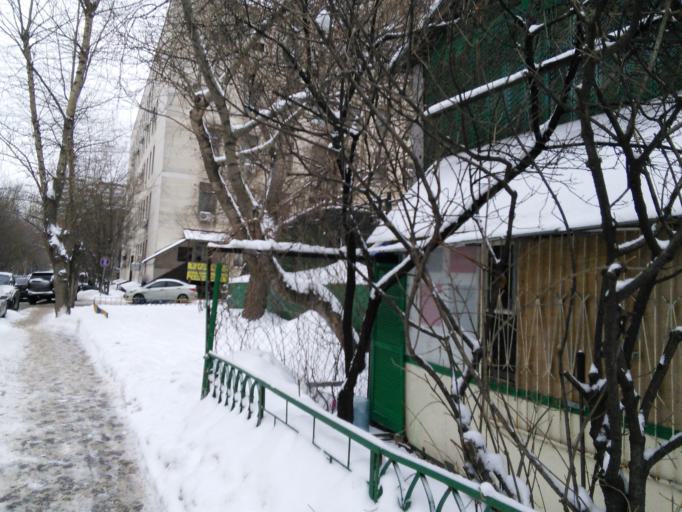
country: RU
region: Moscow
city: Mar'ina Roshcha
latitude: 55.8071
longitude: 37.6344
